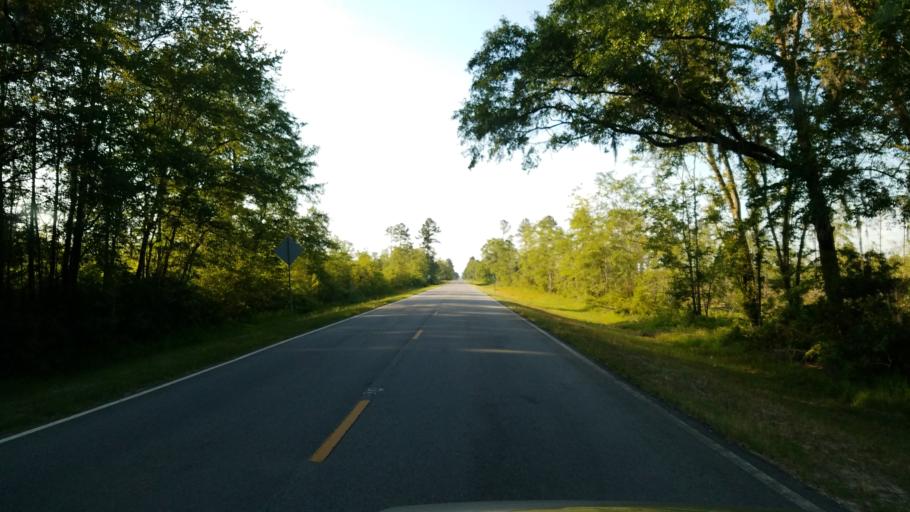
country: US
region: Georgia
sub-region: Lanier County
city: Lakeland
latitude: 31.1446
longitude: -83.0866
